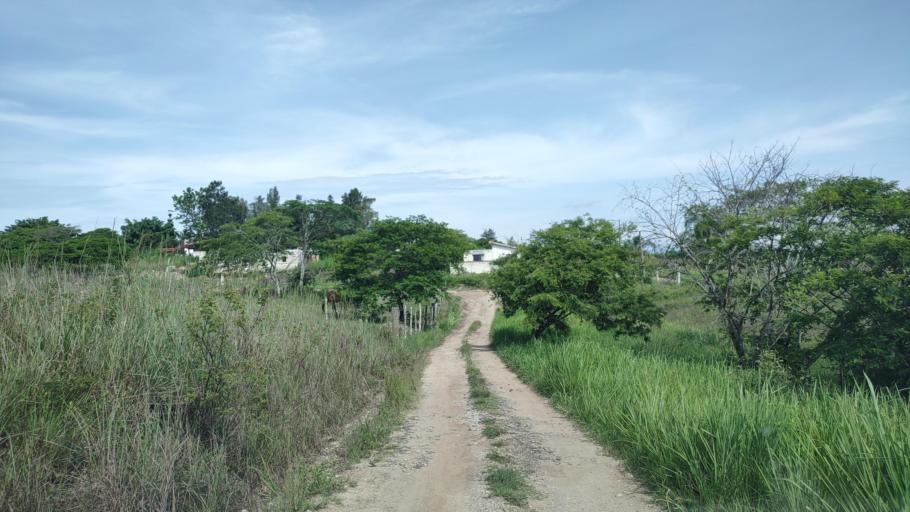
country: MX
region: Veracruz
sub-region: Emiliano Zapata
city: Dos Rios
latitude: 19.4723
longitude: -96.8246
